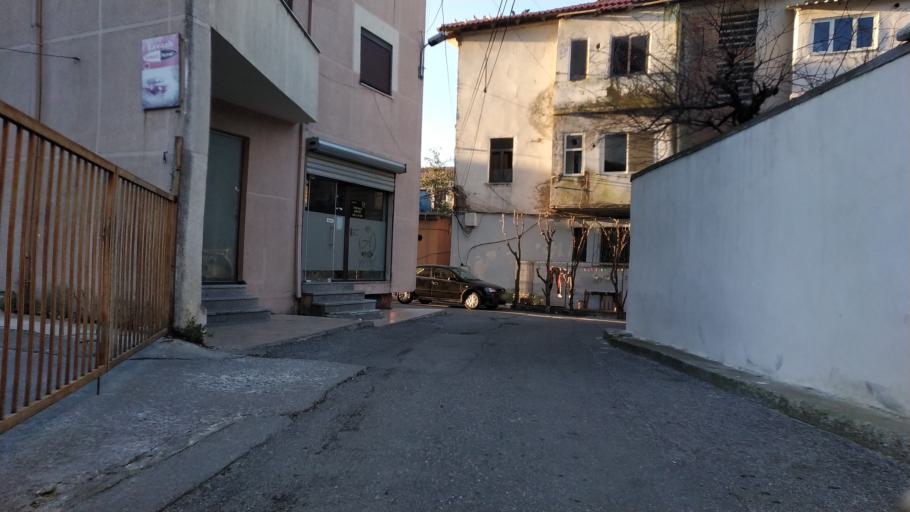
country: AL
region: Shkoder
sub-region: Rrethi i Shkodres
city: Shkoder
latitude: 42.0660
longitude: 19.5159
